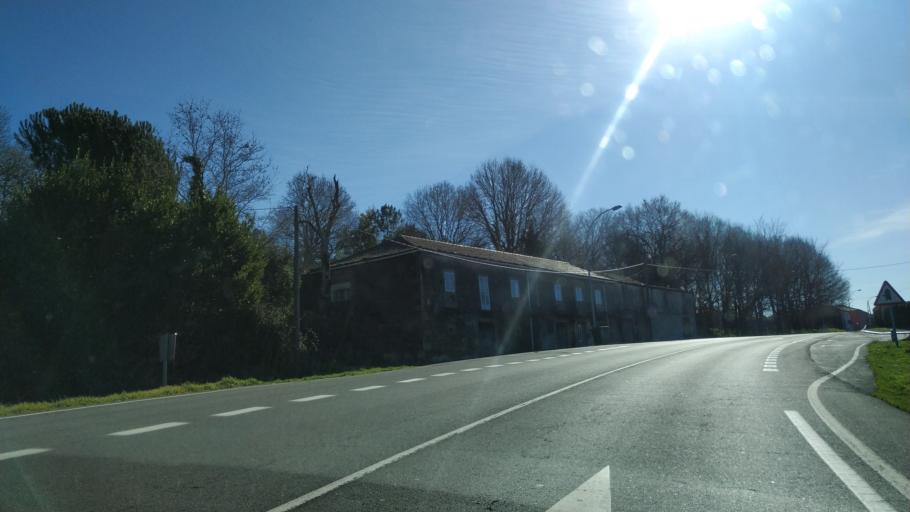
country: ES
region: Galicia
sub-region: Provincia de Pontevedra
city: Lalin
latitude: 42.6817
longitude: -8.1673
